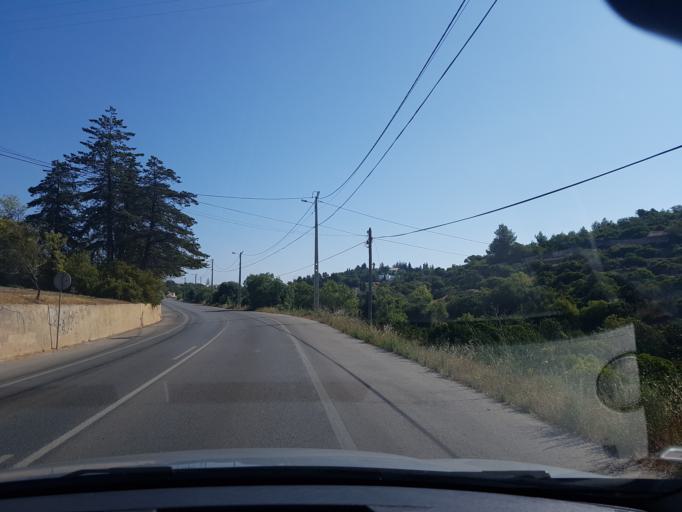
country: PT
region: Faro
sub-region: Lagoa
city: Carvoeiro
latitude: 37.1043
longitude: -8.4635
